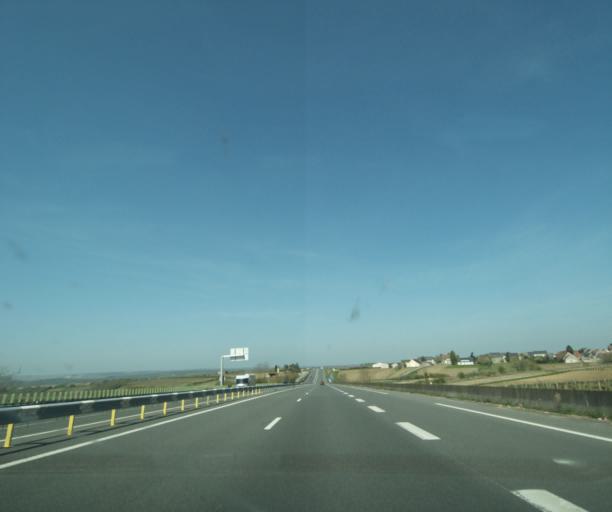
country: FR
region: Bourgogne
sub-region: Departement de la Nievre
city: Pouilly-sur-Loire
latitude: 47.3028
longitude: 2.9494
